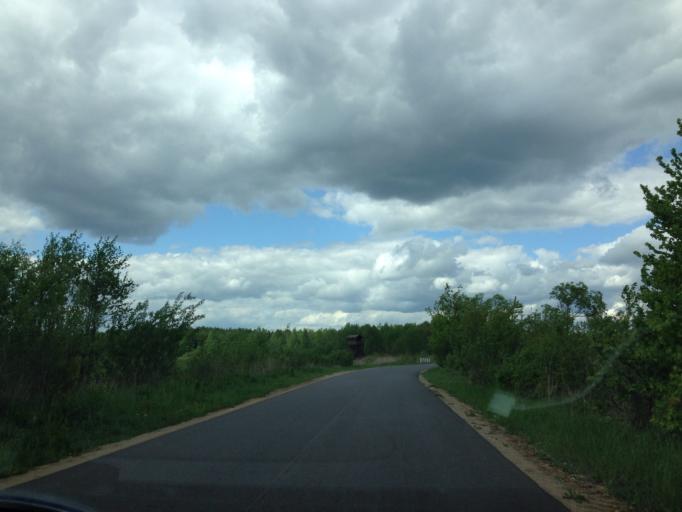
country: PL
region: Podlasie
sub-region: Powiat bialostocki
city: Tykocin
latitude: 53.2975
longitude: 22.6055
